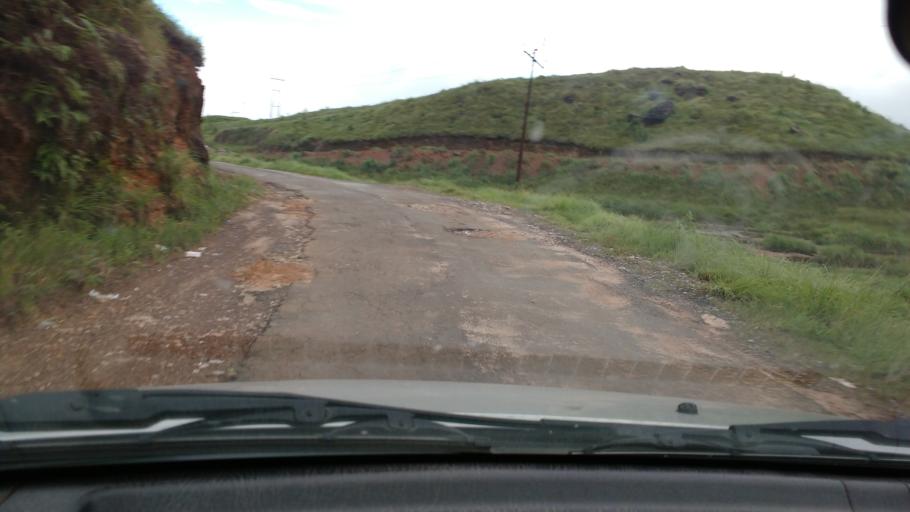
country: IN
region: Meghalaya
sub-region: East Khasi Hills
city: Cherrapunji
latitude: 25.2783
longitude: 91.6929
